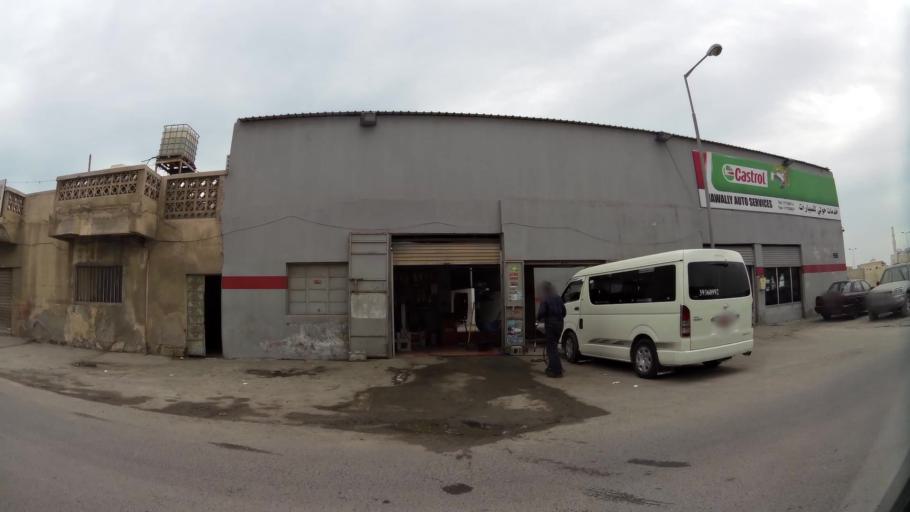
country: BH
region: Northern
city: Sitrah
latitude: 26.1658
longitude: 50.6144
